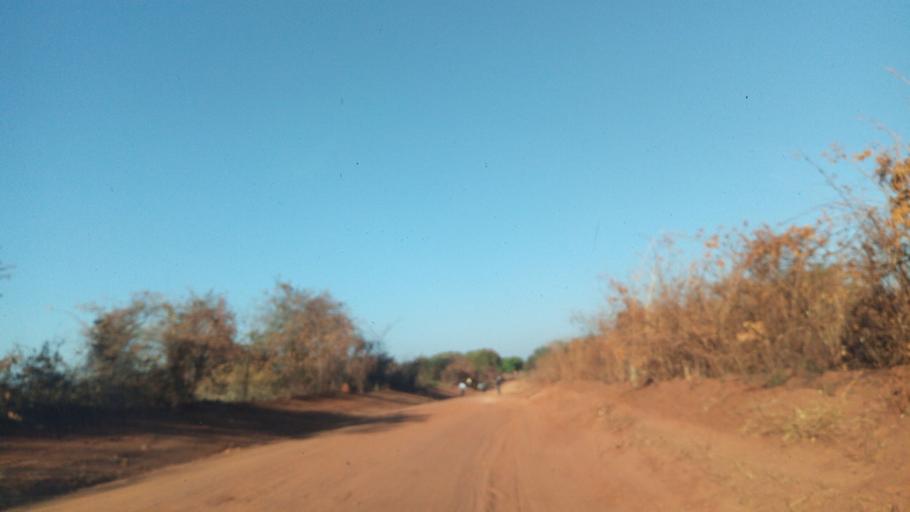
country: ZM
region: Luapula
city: Mwense
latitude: -10.4183
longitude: 28.6066
